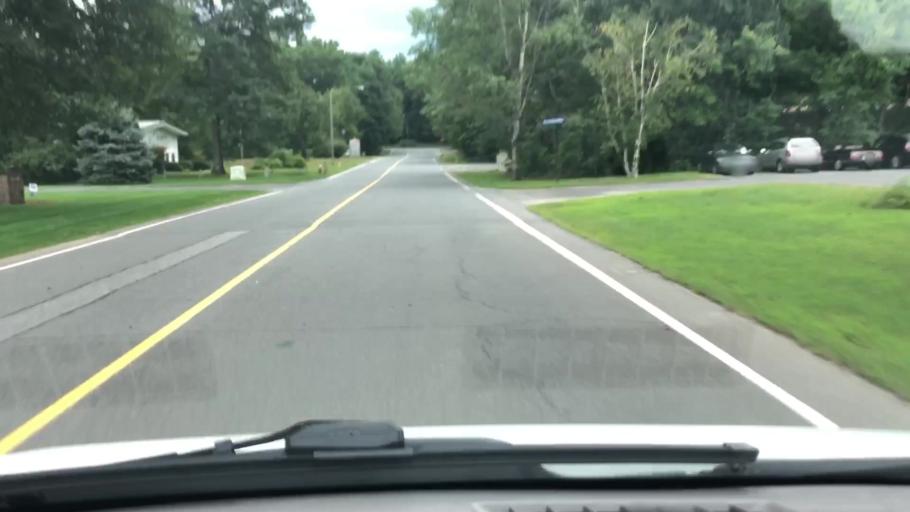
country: US
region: Massachusetts
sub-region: Franklin County
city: Turners Falls
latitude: 42.5919
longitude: -72.5292
